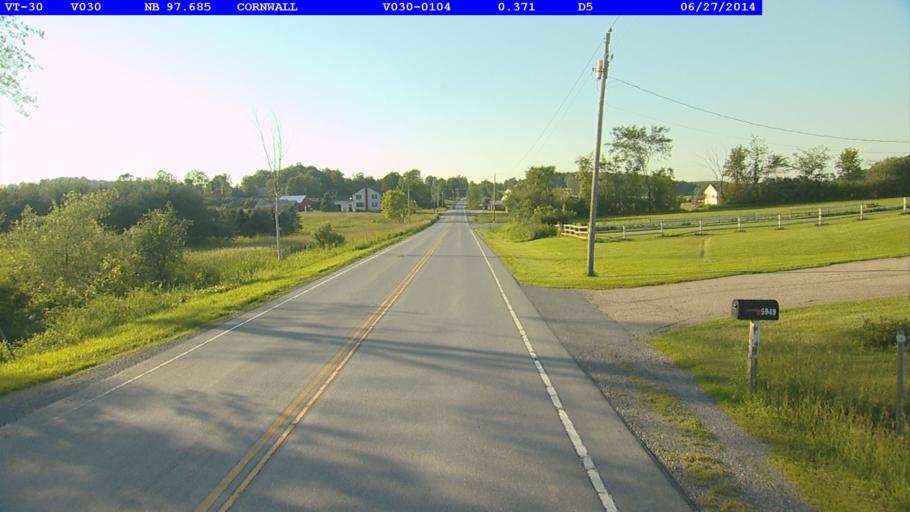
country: US
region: Vermont
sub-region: Addison County
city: Middlebury (village)
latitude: 43.9134
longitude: -73.2088
